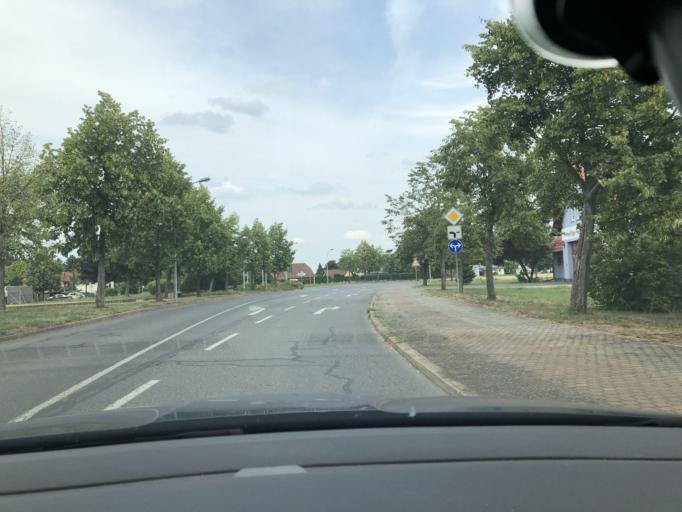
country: DE
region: Brandenburg
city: Kasel-Golzig
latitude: 51.9611
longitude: 13.7457
